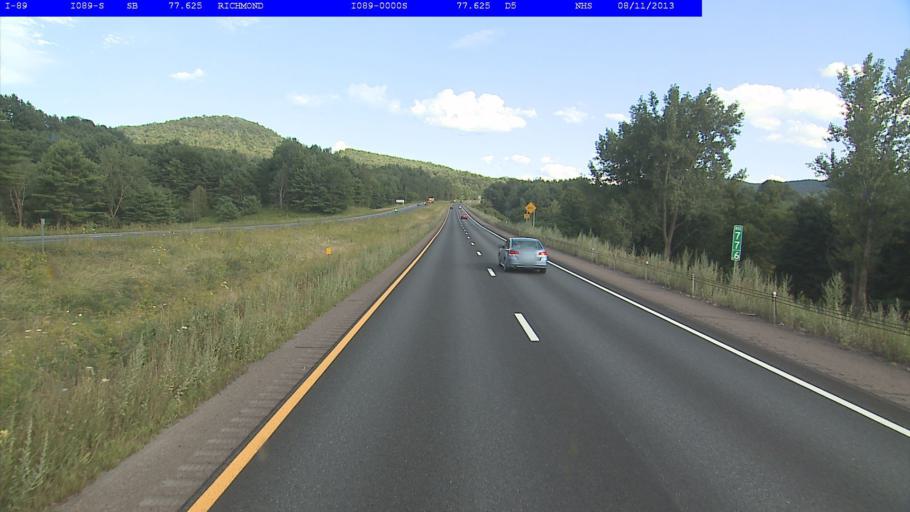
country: US
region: Vermont
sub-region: Chittenden County
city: Williston
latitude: 44.4177
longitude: -72.9978
